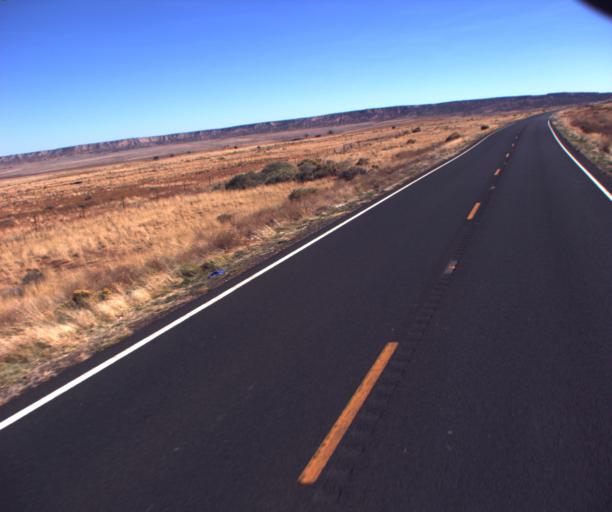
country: US
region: Arizona
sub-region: Apache County
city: Ganado
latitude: 35.7810
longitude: -109.6609
